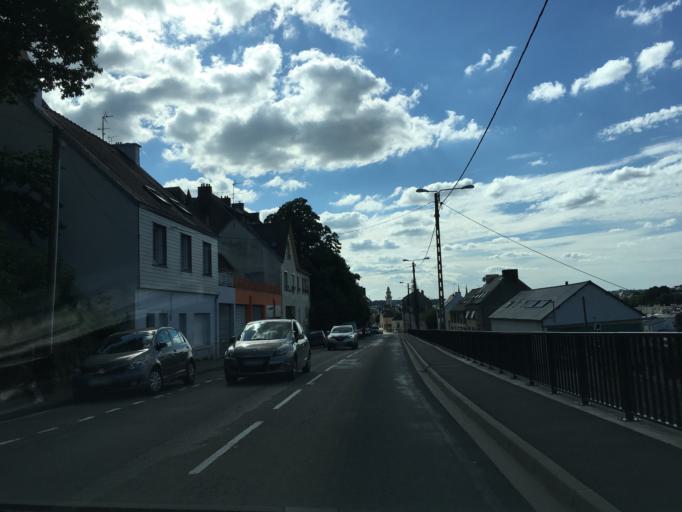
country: FR
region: Brittany
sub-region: Departement du Finistere
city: Quimper
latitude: 47.9923
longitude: -4.0855
